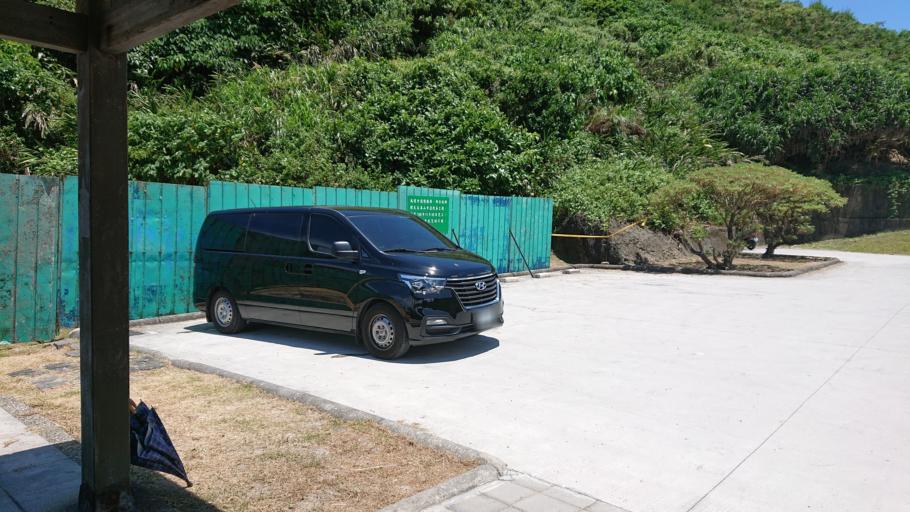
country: TW
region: Taiwan
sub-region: Hualien
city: Hualian
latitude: 23.6990
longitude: 121.5512
